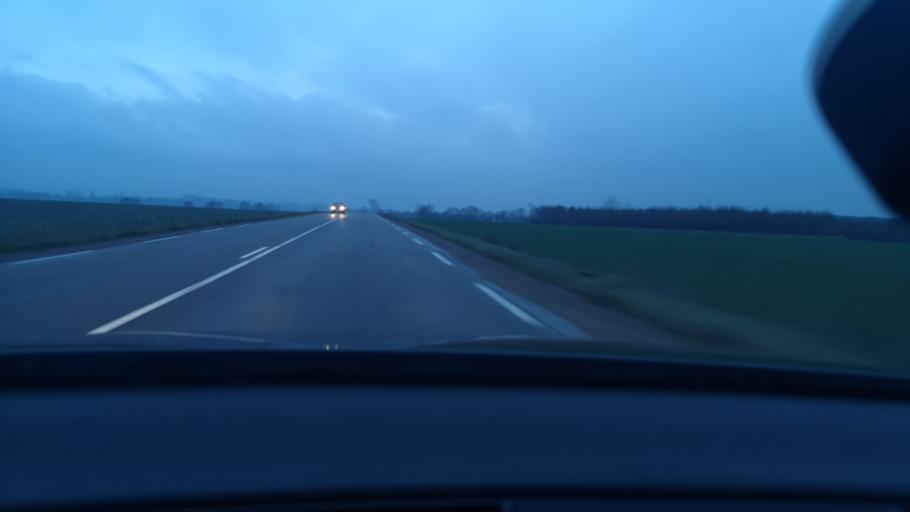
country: FR
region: Bourgogne
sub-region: Departement de Saone-et-Loire
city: Verdun-sur-le-Doubs
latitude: 47.0081
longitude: 4.9621
